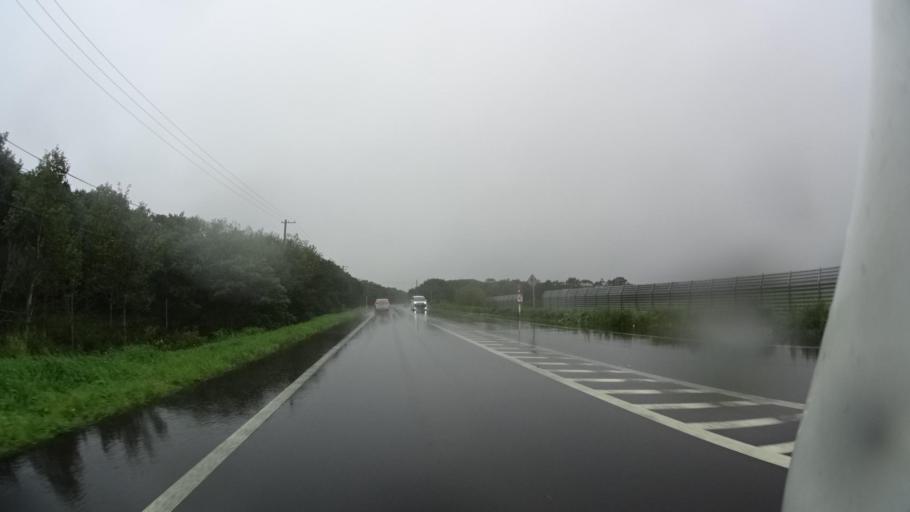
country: JP
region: Hokkaido
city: Nemuro
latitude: 43.2373
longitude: 145.2728
